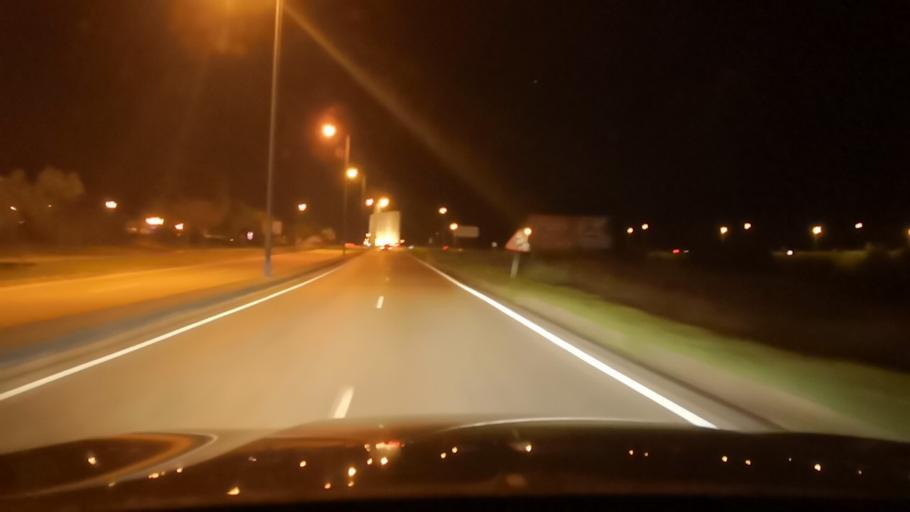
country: PT
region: Setubal
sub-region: Montijo
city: Montijo
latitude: 38.6997
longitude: -8.9444
